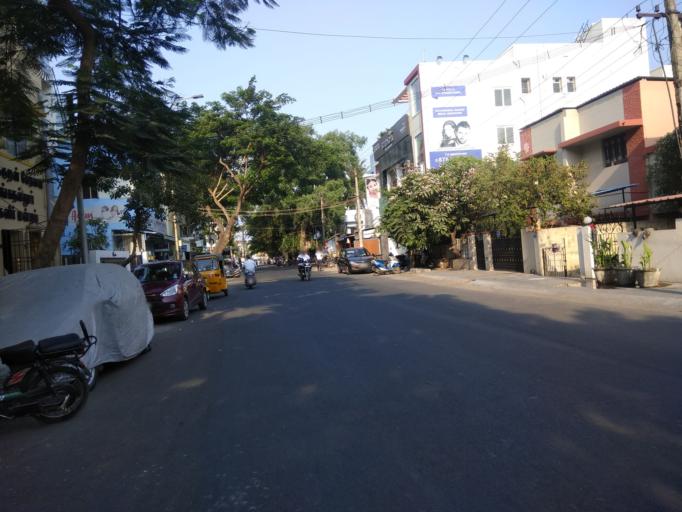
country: IN
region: Tamil Nadu
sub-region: Kancheepuram
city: Madipakkam
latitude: 12.9807
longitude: 80.1877
